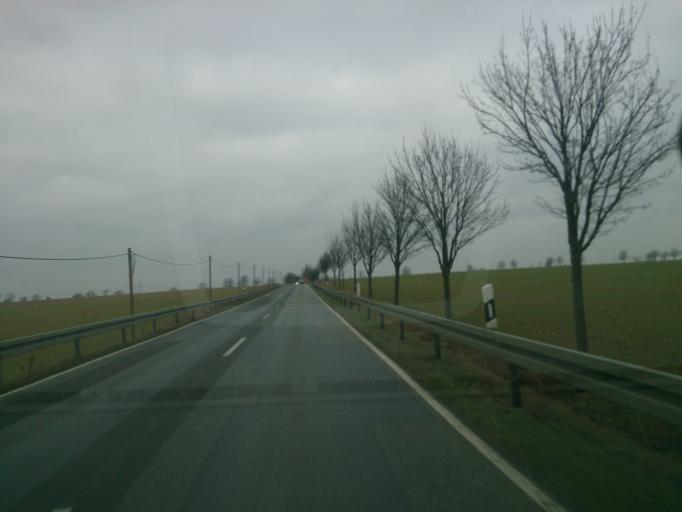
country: DE
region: Mecklenburg-Vorpommern
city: Borrentin
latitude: 53.7727
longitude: 12.9405
